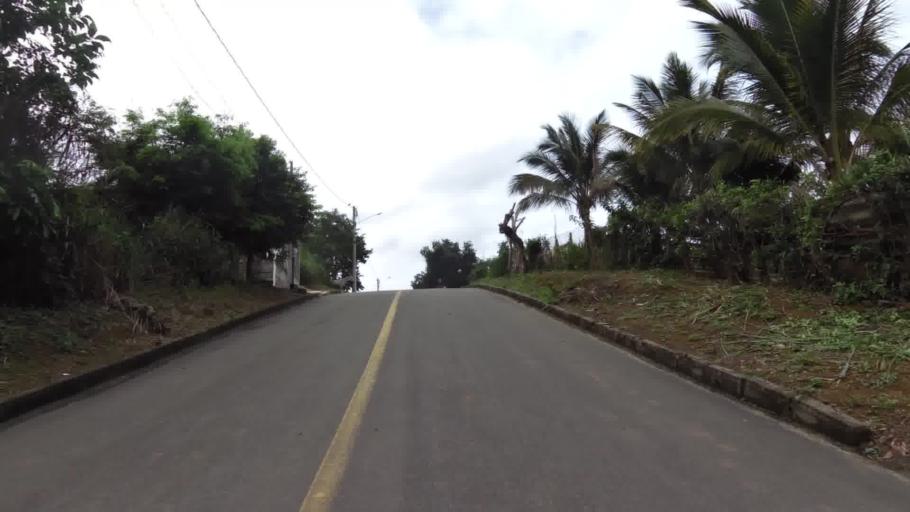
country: BR
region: Espirito Santo
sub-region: Piuma
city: Piuma
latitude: -20.7972
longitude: -40.6437
